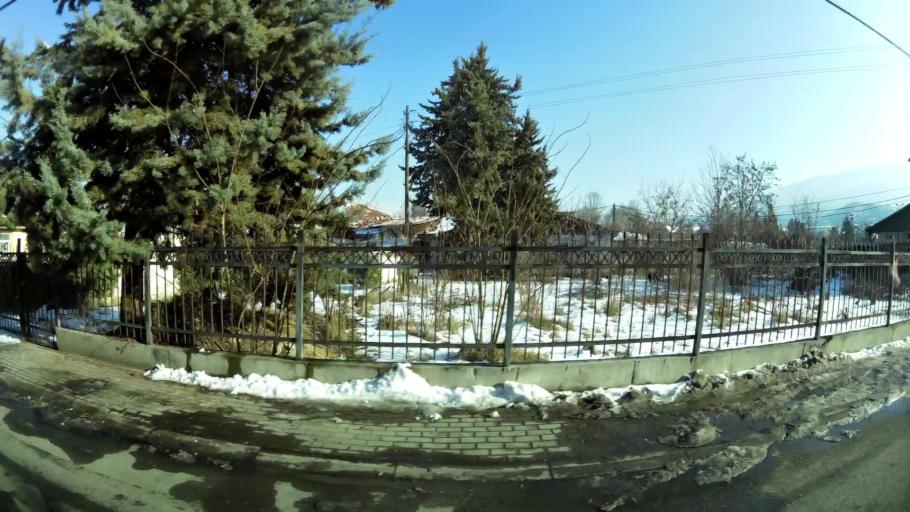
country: MK
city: Krushopek
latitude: 42.0025
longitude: 21.3818
